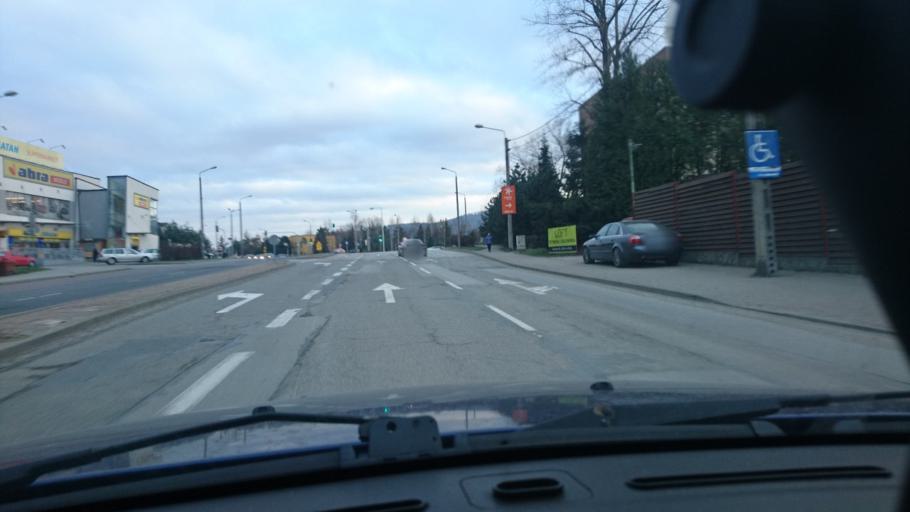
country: PL
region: Silesian Voivodeship
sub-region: Bielsko-Biala
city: Bielsko-Biala
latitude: 49.8065
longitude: 19.0559
